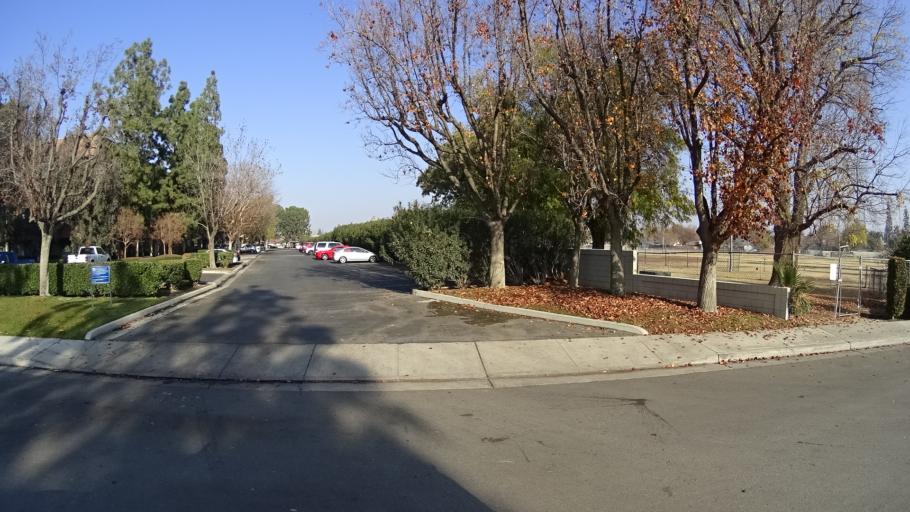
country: US
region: California
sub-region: Kern County
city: Bakersfield
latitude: 35.3609
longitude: -119.0572
